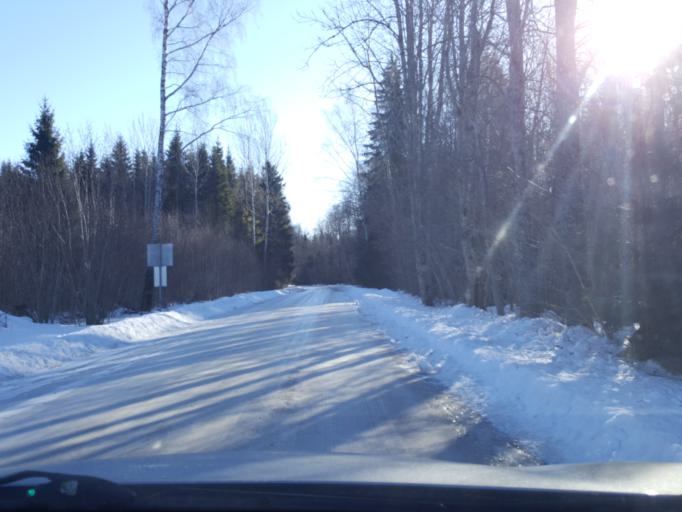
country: EE
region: Viljandimaa
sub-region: Suure-Jaani vald
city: Suure-Jaani
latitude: 58.4640
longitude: 25.5478
